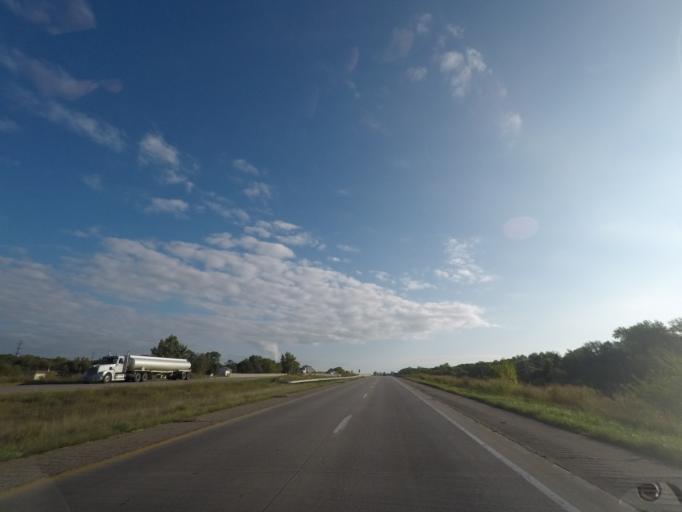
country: US
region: Iowa
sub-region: Polk County
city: Pleasant Hill
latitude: 41.5812
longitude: -93.5092
